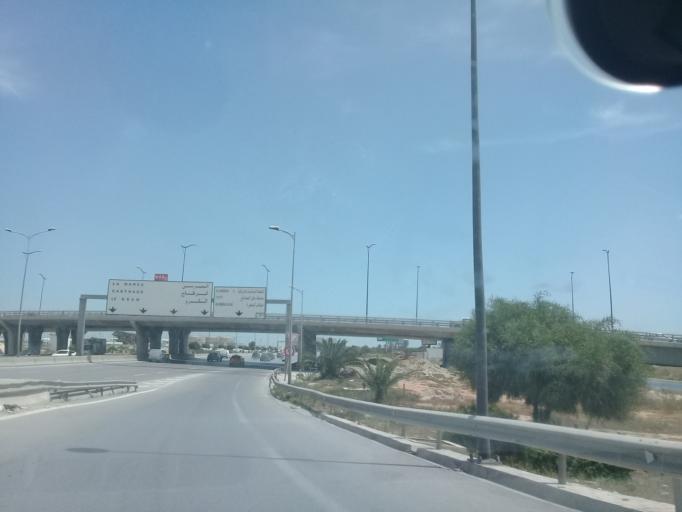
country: TN
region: Ariana
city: Ariana
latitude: 36.8316
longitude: 10.2149
